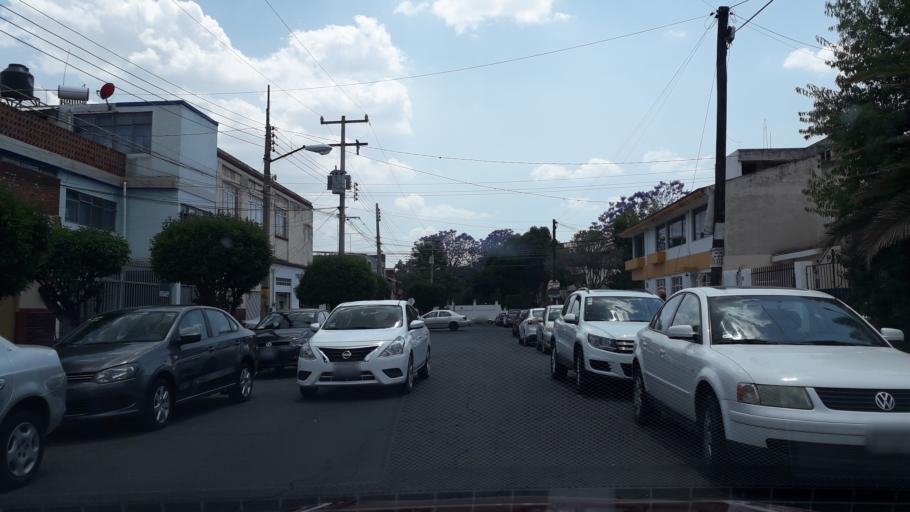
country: MX
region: Puebla
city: Puebla
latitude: 19.0376
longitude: -98.2160
